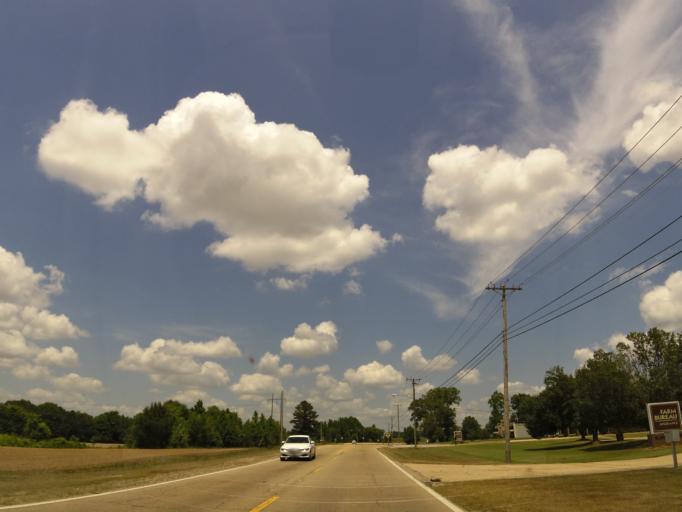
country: US
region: Mississippi
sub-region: Lee County
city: Tupelo
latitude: 34.2791
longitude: -88.6805
